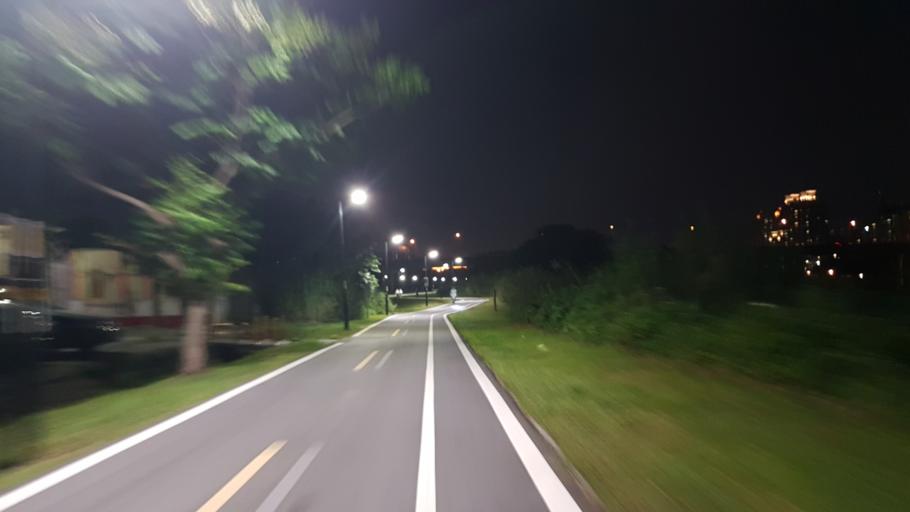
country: TW
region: Taipei
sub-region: Taipei
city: Banqiao
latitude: 24.9685
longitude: 121.5291
